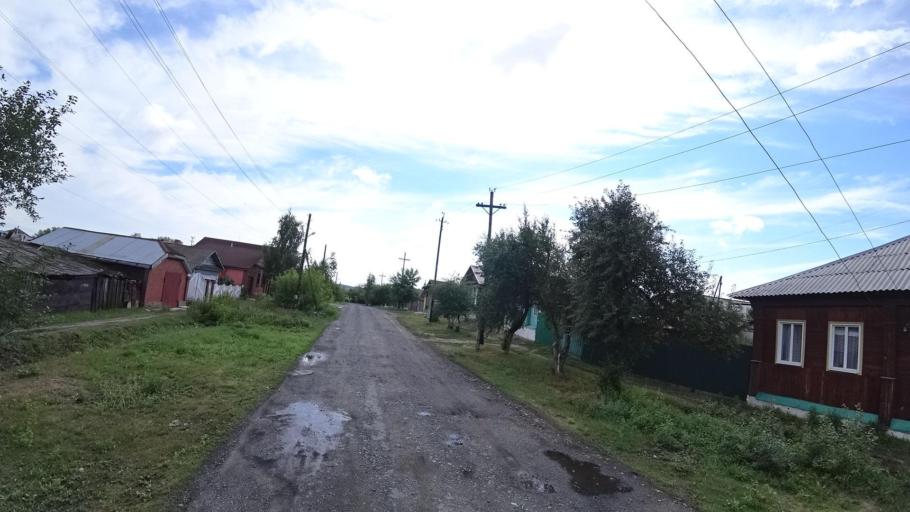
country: RU
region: Sverdlovsk
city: Kamyshlov
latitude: 56.8401
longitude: 62.7076
